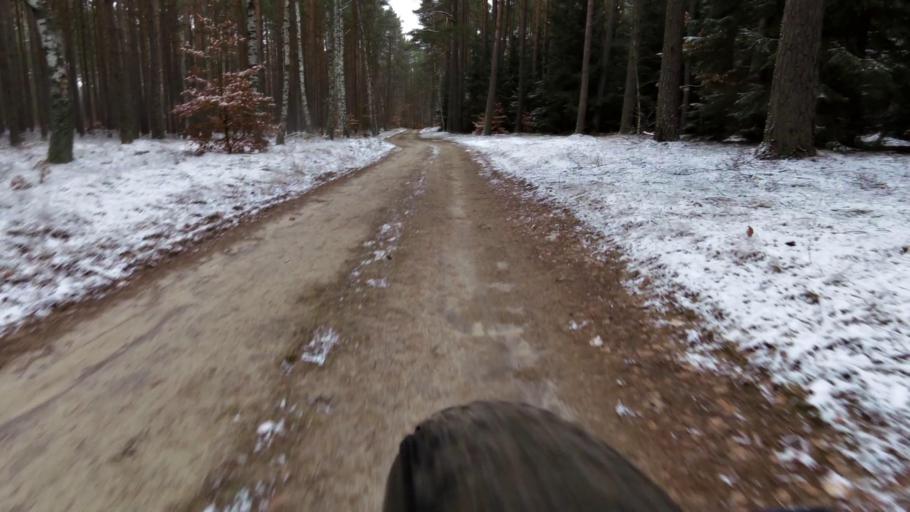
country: PL
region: West Pomeranian Voivodeship
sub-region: Powiat walecki
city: Miroslawiec
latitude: 53.3089
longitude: 16.0678
